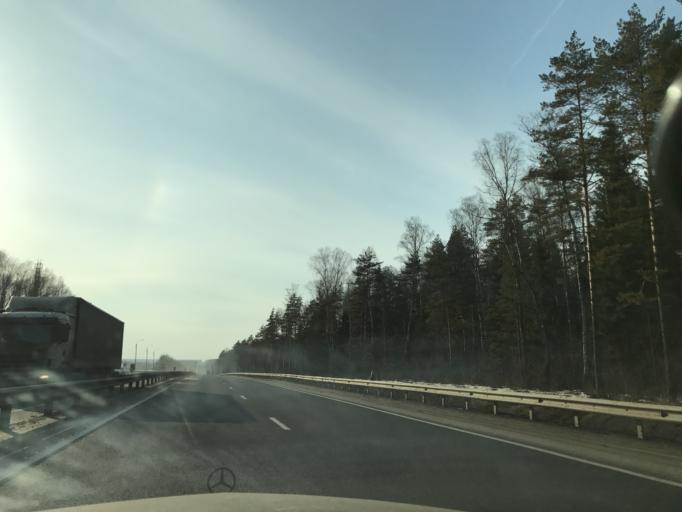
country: RU
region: Vladimir
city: Melekhovo
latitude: 56.2135
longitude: 41.3534
